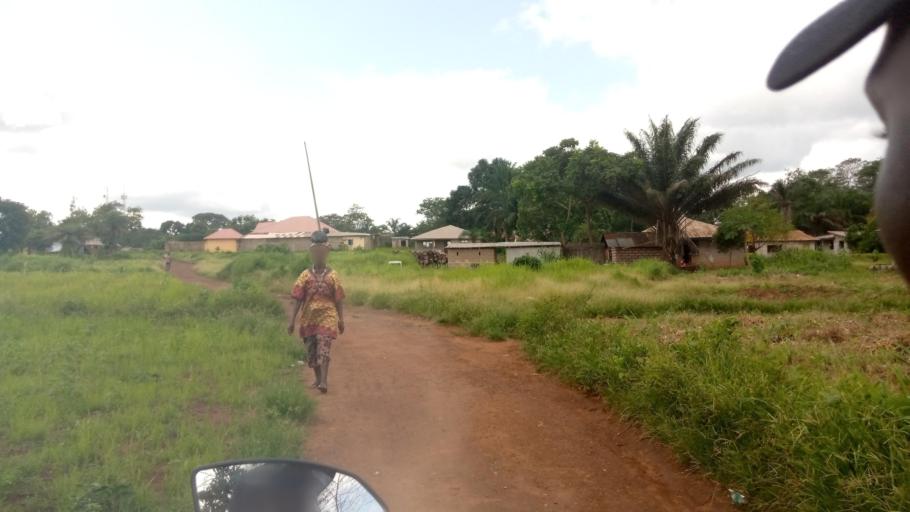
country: SL
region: Northern Province
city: Kamakwie
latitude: 9.4917
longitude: -12.2344
